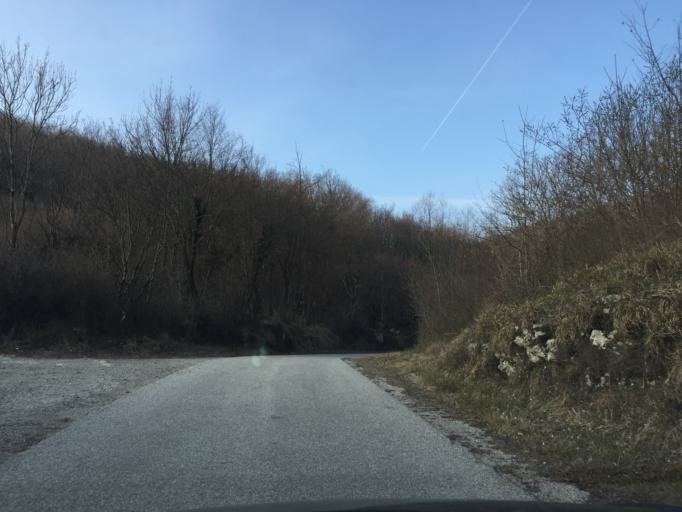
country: SI
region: Kanal
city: Kanal
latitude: 46.0591
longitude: 13.6670
